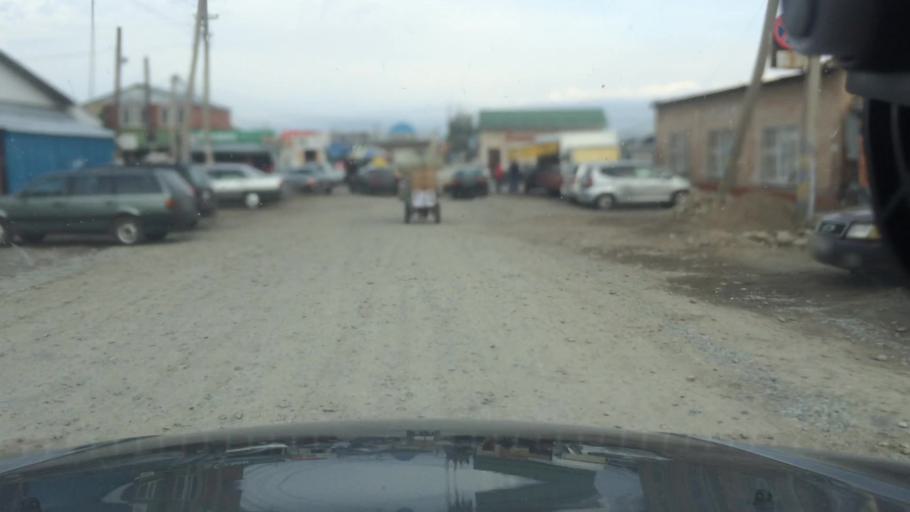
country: KG
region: Ysyk-Koel
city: Karakol
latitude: 42.4918
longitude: 78.3859
